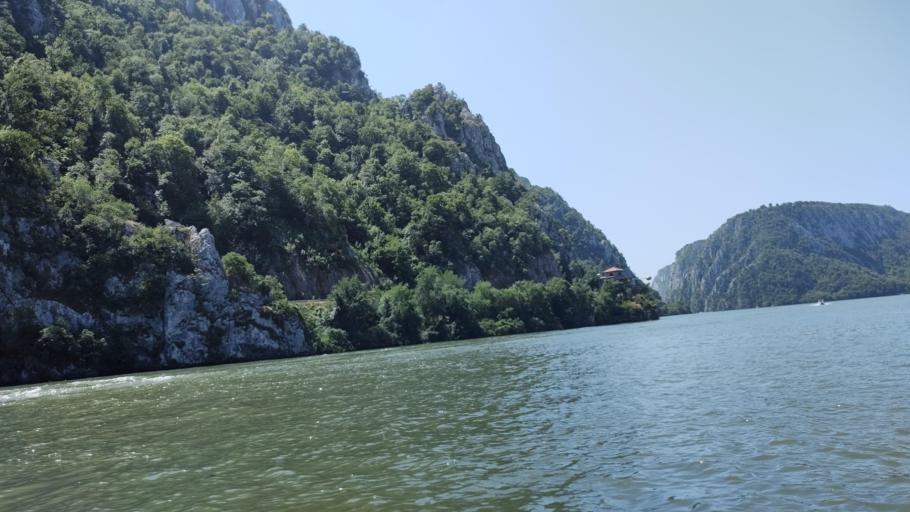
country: RO
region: Mehedinti
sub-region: Comuna Dubova
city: Dubova
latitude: 44.6278
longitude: 22.2805
